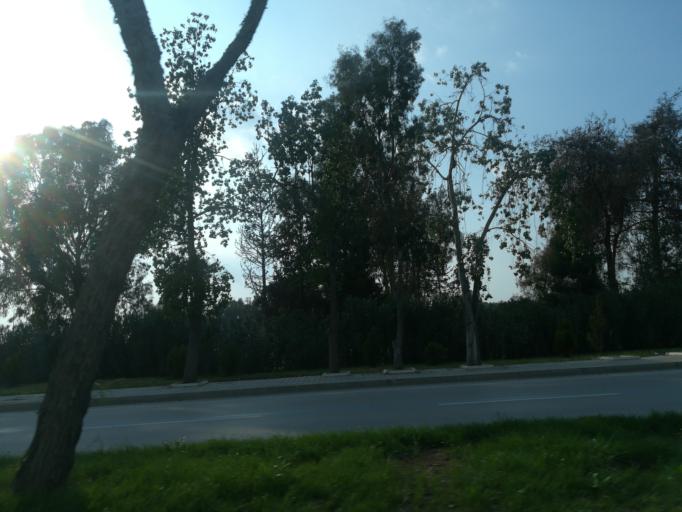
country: TR
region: Adana
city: Adana
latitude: 37.0258
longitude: 35.3441
